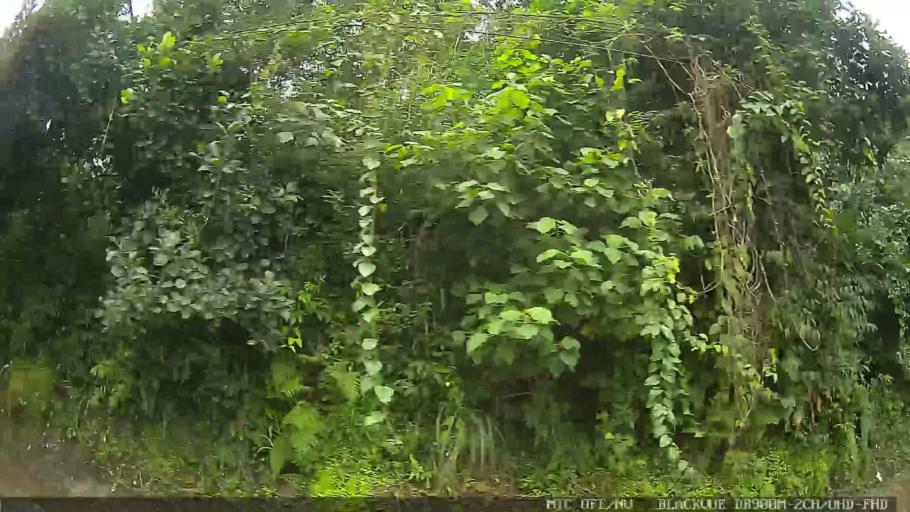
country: BR
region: Sao Paulo
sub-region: Guaruja
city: Guaruja
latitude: -23.9959
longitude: -46.2698
